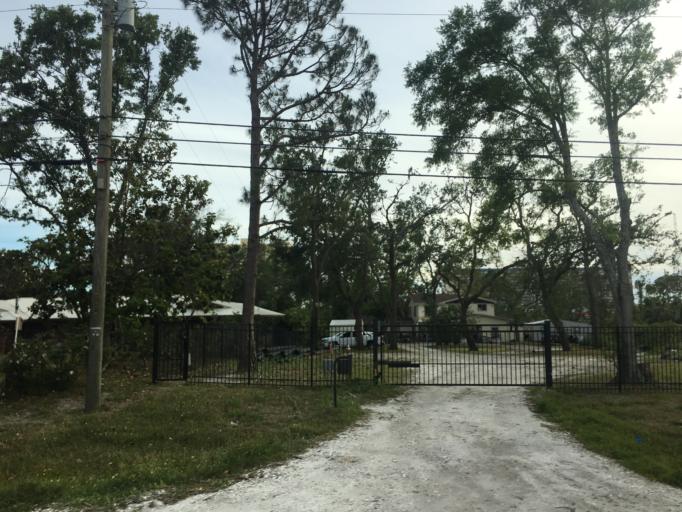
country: US
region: Florida
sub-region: Bay County
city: Panama City Beach
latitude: 30.1712
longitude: -85.7881
